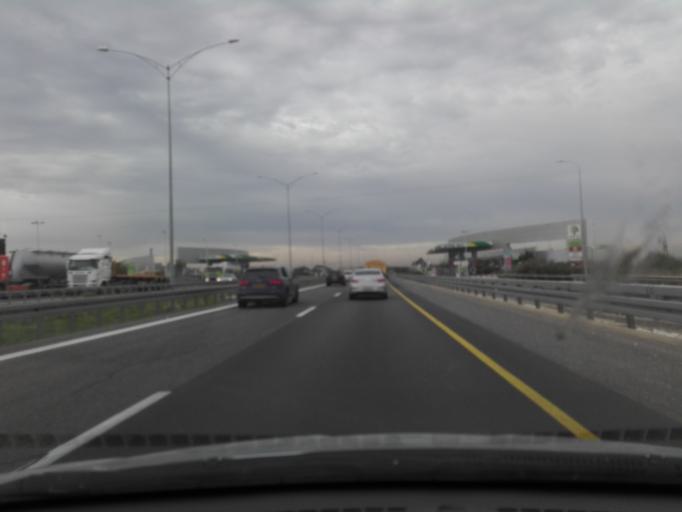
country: IL
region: Central District
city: Mazkeret Batya
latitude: 31.8838
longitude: 34.8796
